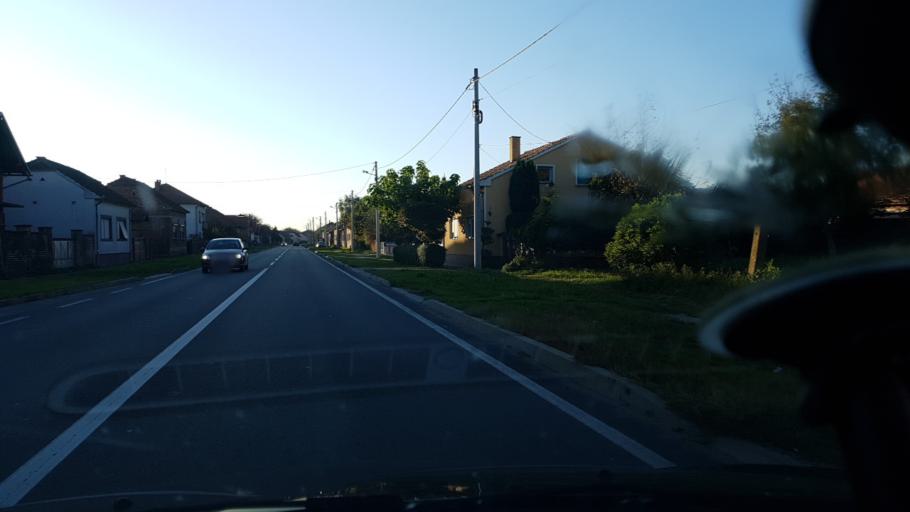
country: HR
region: Koprivnicko-Krizevacka
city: Virje
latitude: 46.0604
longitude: 17.0054
